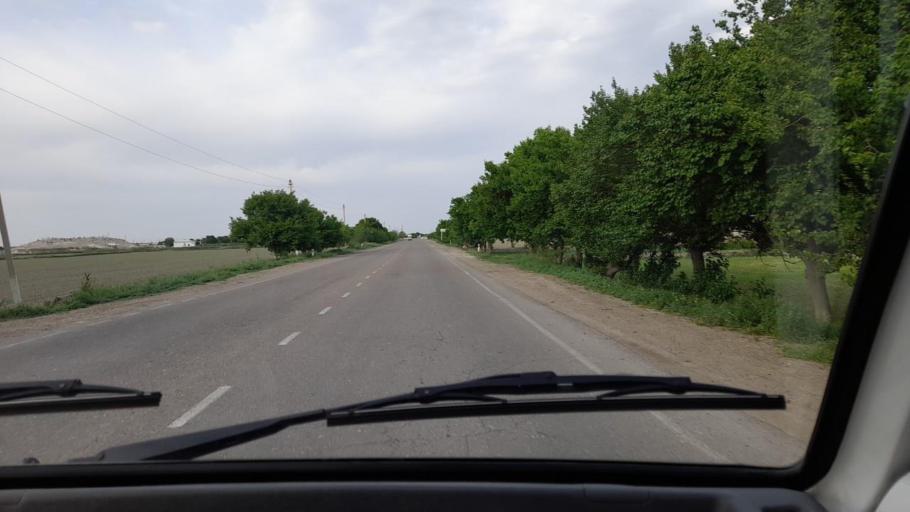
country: UZ
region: Bukhara
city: Romiton
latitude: 39.9798
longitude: 64.3094
